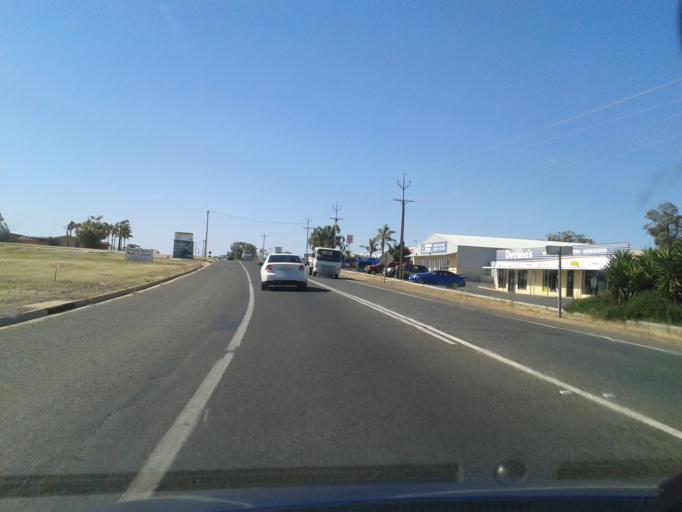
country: AU
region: South Australia
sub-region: Berri and Barmera
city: Berri
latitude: -34.2633
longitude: 140.6139
